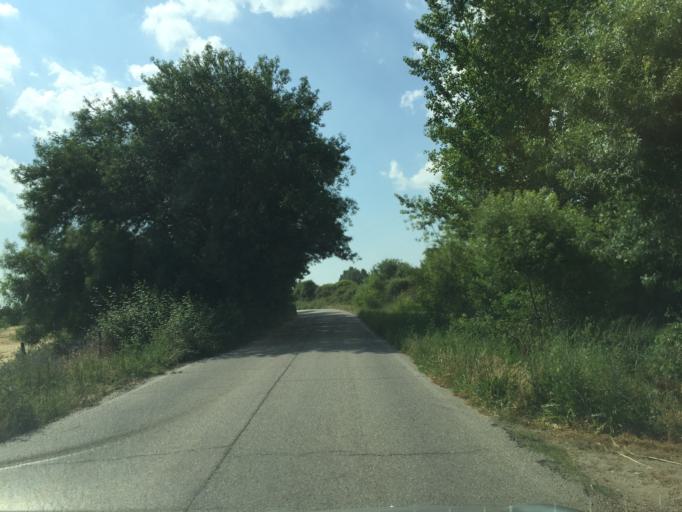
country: PT
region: Santarem
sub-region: Alpiarca
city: Alpiarca
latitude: 39.3028
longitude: -8.5656
